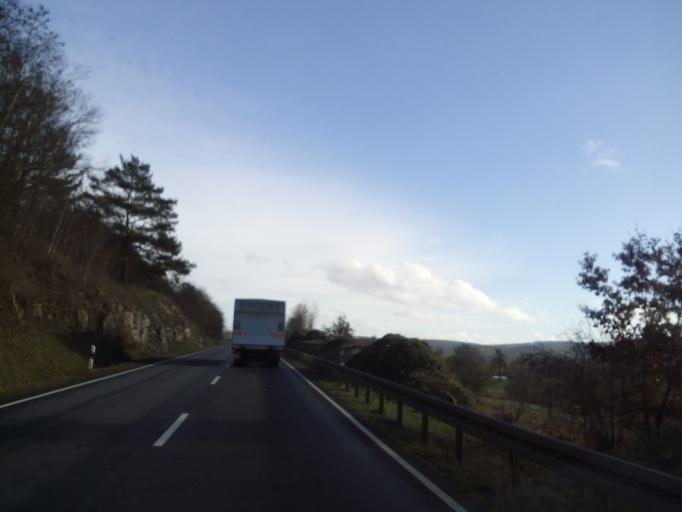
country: DE
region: Bavaria
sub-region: Upper Franconia
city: Altenkunstadt
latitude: 50.1310
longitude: 11.2589
